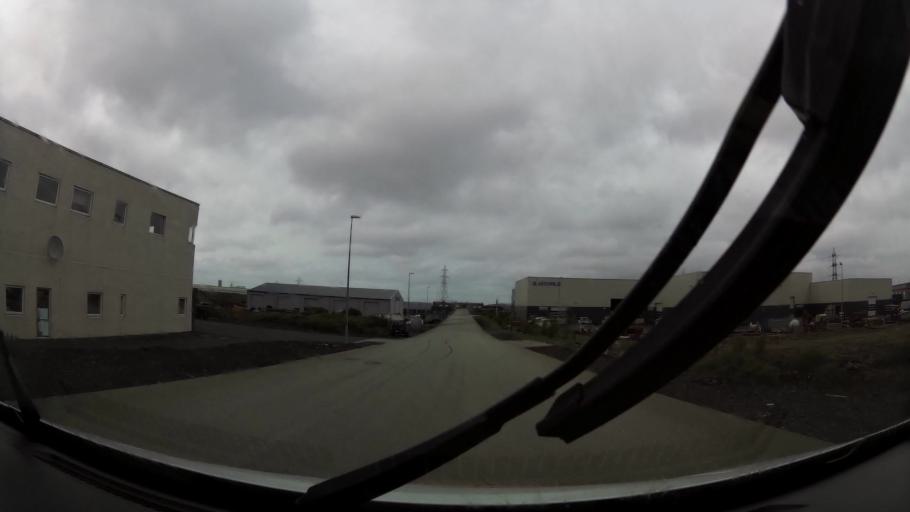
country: IS
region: Capital Region
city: Alftanes
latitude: 64.0401
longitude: -22.0015
